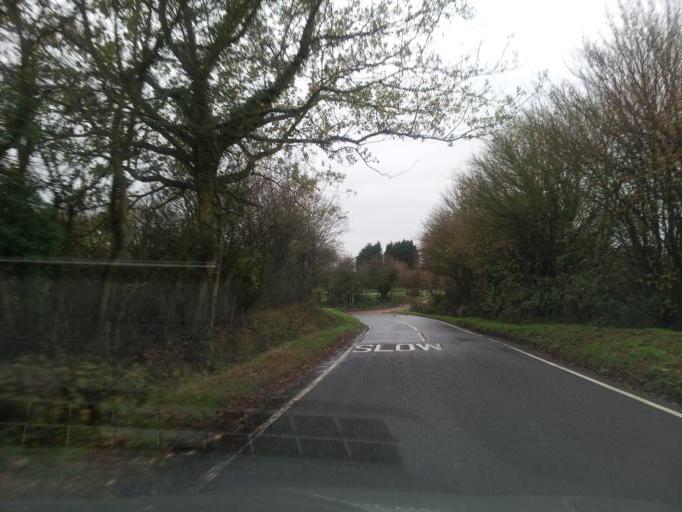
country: GB
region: England
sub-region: Essex
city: Eight Ash Green
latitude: 51.9141
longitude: 0.7925
